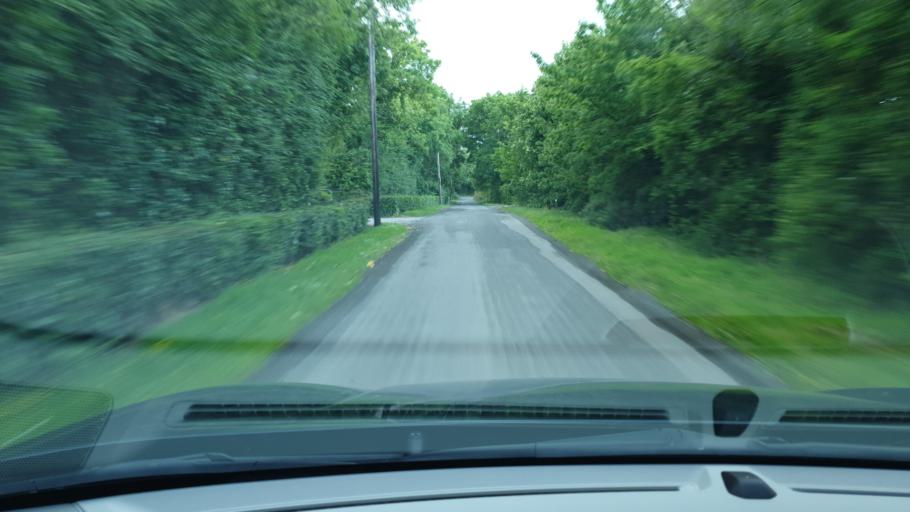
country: IE
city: Kentstown
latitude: 53.5733
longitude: -6.5093
